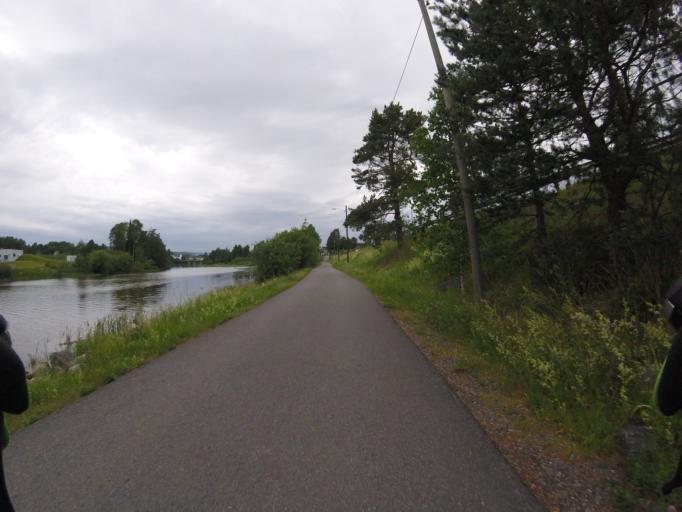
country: NO
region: Akershus
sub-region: Skedsmo
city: Lillestrom
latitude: 59.9783
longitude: 11.0168
